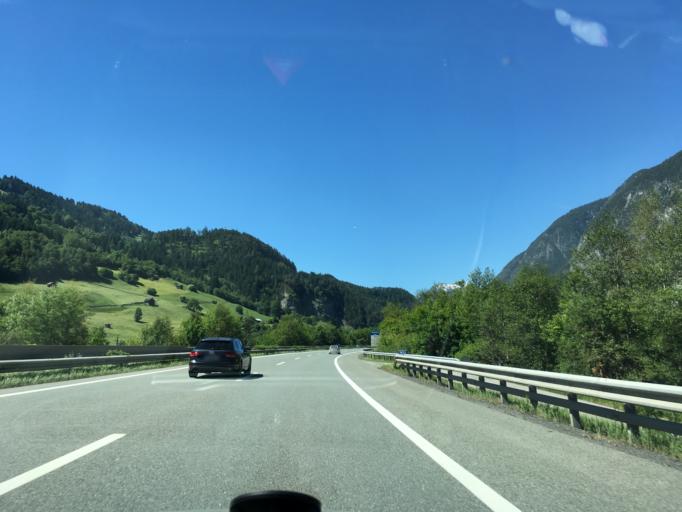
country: AT
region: Tyrol
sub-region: Politischer Bezirk Landeck
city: Zams
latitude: 47.1762
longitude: 10.6148
